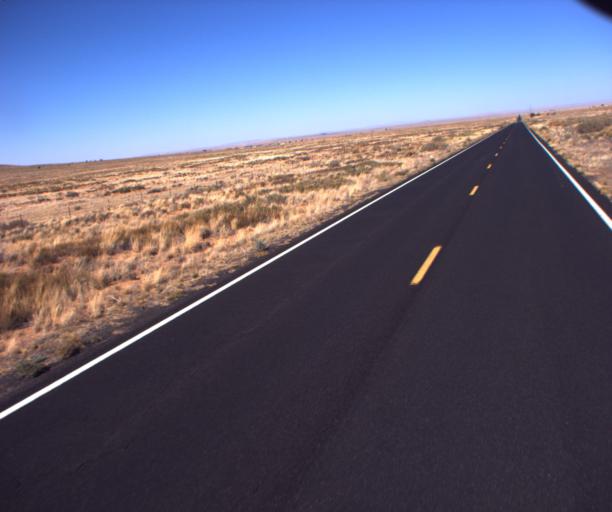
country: US
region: Arizona
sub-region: Navajo County
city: Dilkon
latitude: 35.4793
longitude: -110.4268
